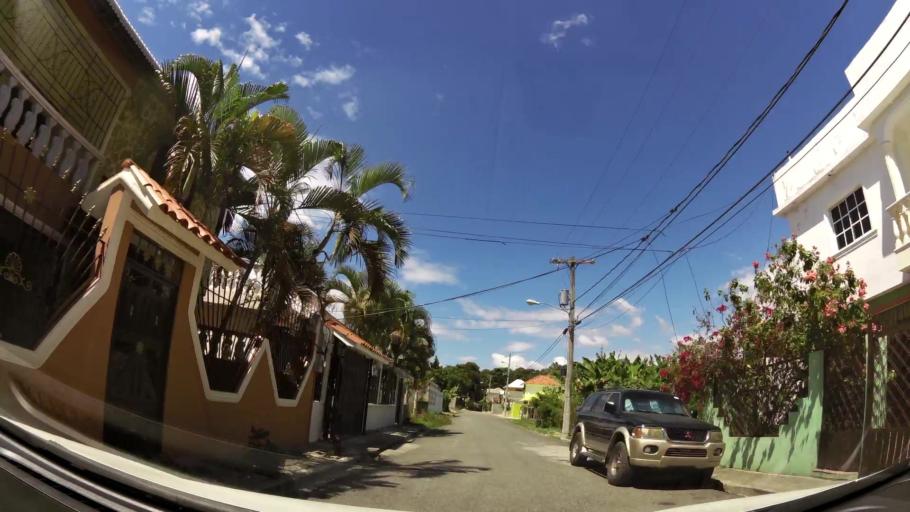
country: DO
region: San Cristobal
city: San Cristobal
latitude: 18.4183
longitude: -70.0906
